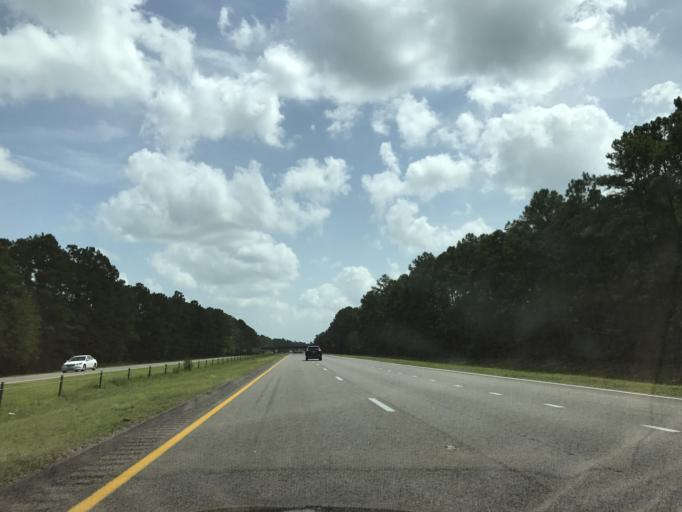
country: US
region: North Carolina
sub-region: Pender County
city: Burgaw
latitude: 34.5714
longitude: -77.9002
